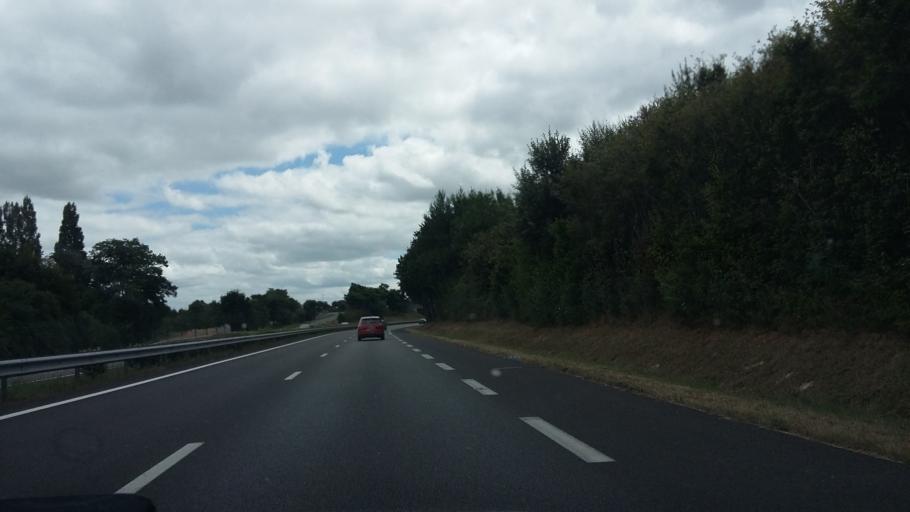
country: FR
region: Pays de la Loire
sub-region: Departement de la Vendee
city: Challans
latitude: 46.8546
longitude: -1.8526
